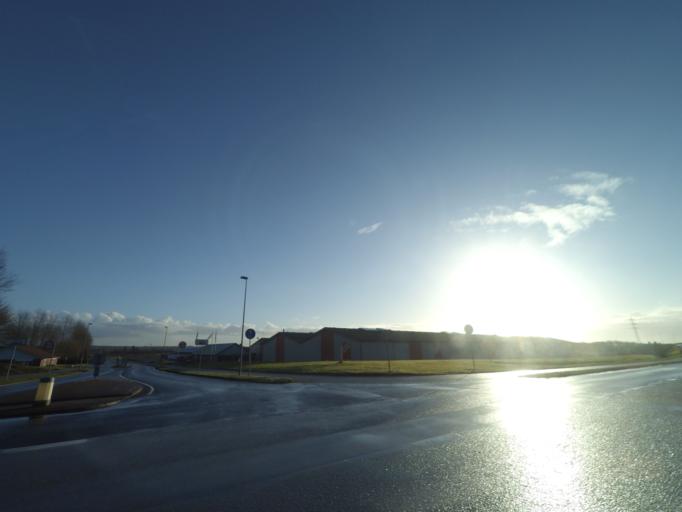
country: DK
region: Central Jutland
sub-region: Ikast-Brande Kommune
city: Ikast
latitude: 56.1189
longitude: 9.1381
